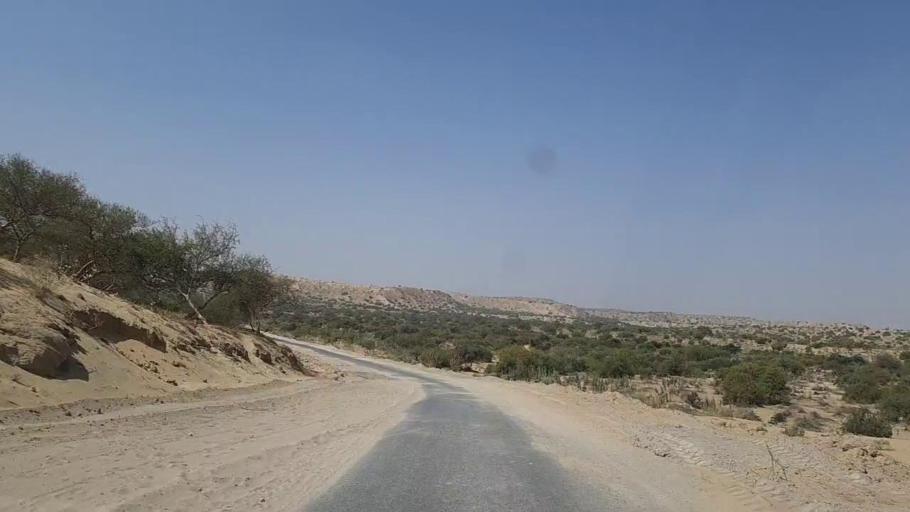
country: PK
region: Sindh
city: Diplo
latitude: 24.5871
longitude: 69.5329
